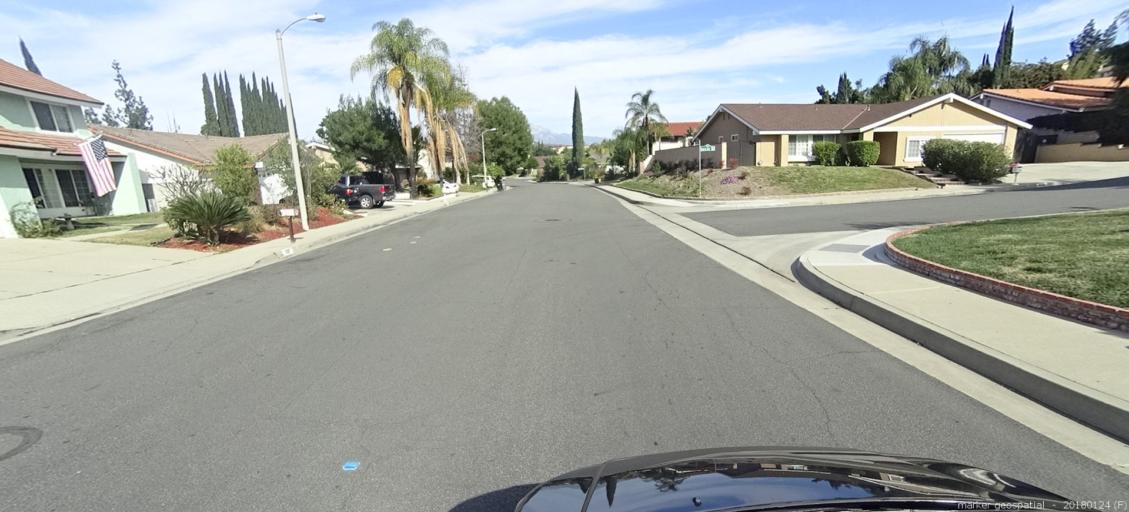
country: US
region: California
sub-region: Los Angeles County
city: Diamond Bar
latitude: 34.0143
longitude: -117.8152
